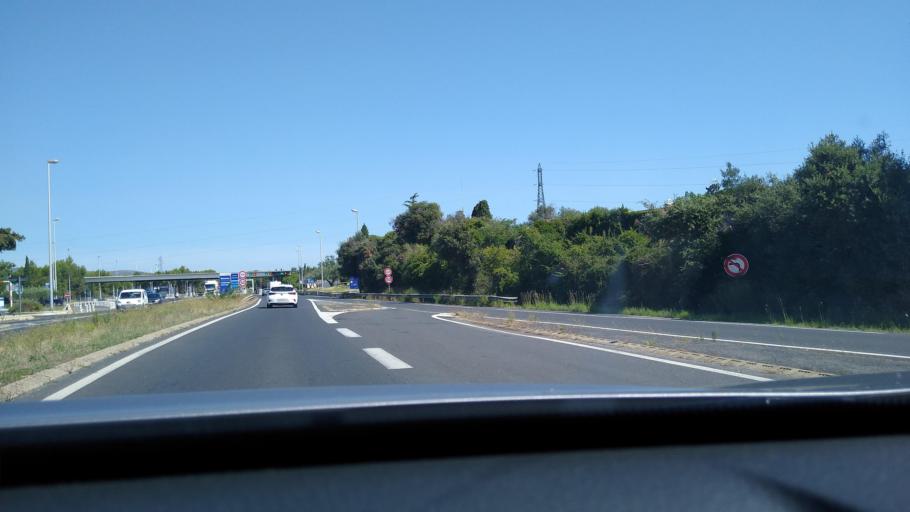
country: FR
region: Languedoc-Roussillon
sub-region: Departement de l'Herault
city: Balaruc-le-Vieux
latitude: 43.4756
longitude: 3.6860
